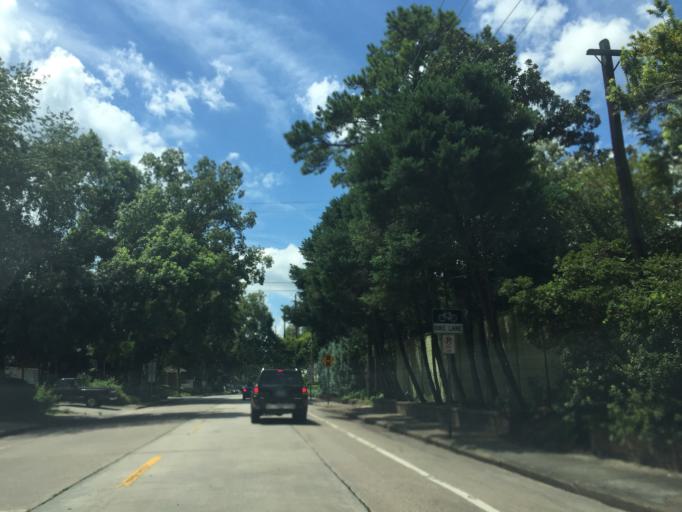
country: US
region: Georgia
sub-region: Chatham County
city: Savannah
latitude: 32.0498
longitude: -81.0980
